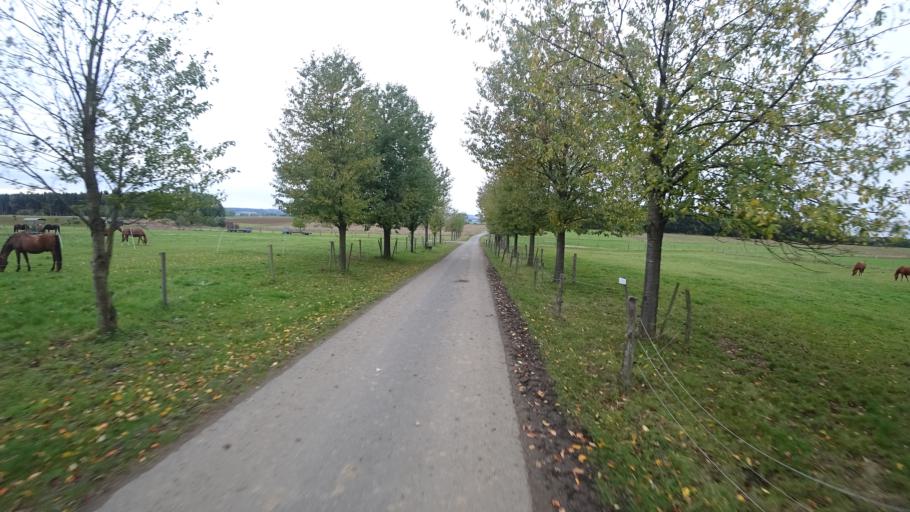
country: DE
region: Rheinland-Pfalz
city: Marienrachdorf
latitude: 50.5497
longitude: 7.7032
